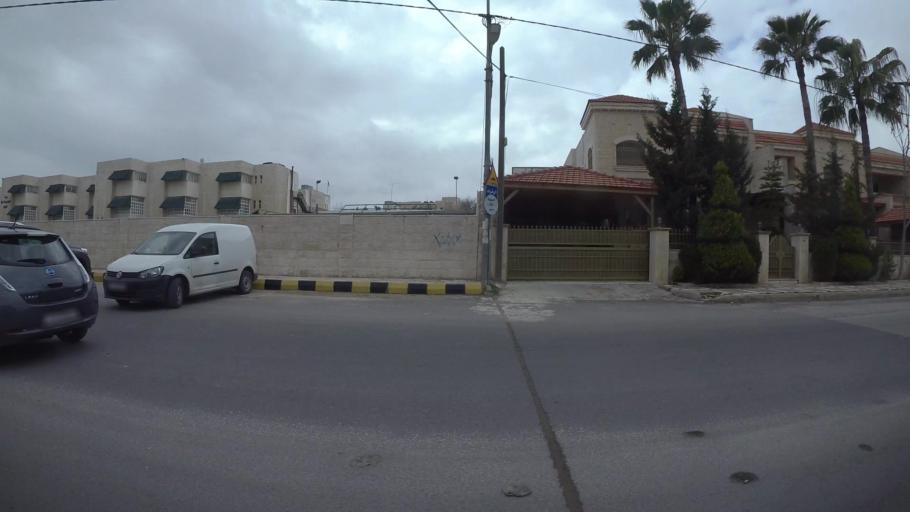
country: JO
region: Amman
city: Wadi as Sir
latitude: 31.9871
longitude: 35.8369
